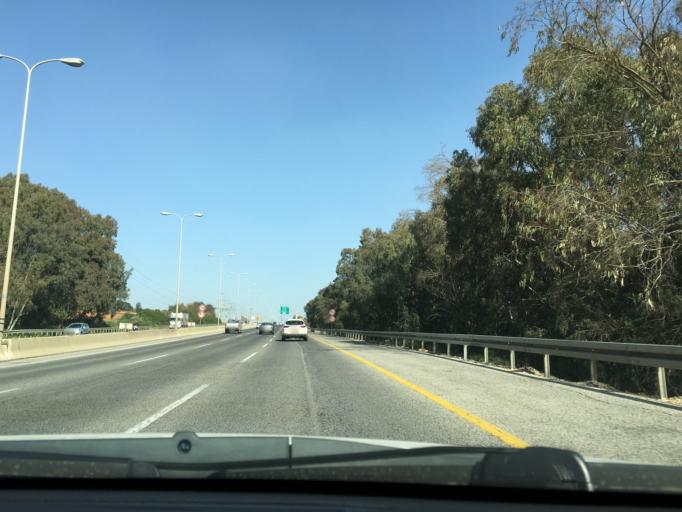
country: IL
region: Central District
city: Hod HaSharon
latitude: 32.1591
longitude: 34.8760
